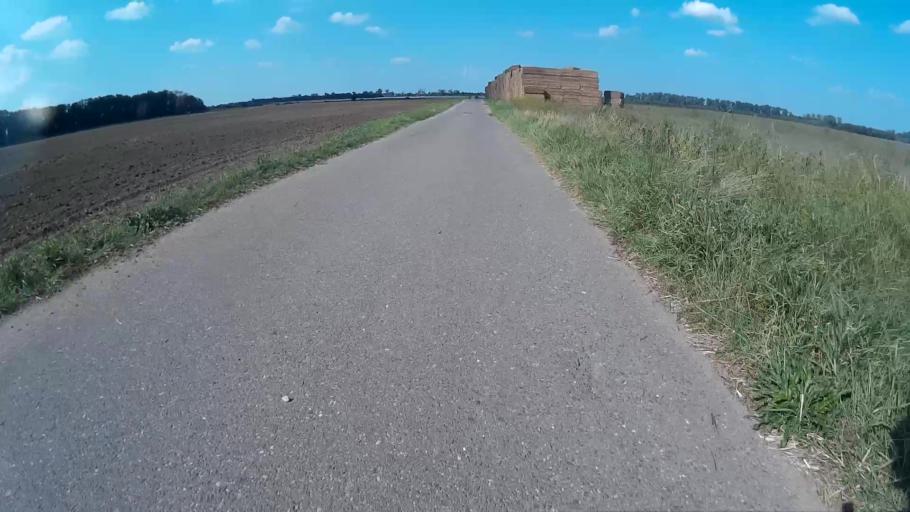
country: CZ
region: South Moravian
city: Hrusovany nad Jevisovkou
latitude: 48.8036
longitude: 16.4275
